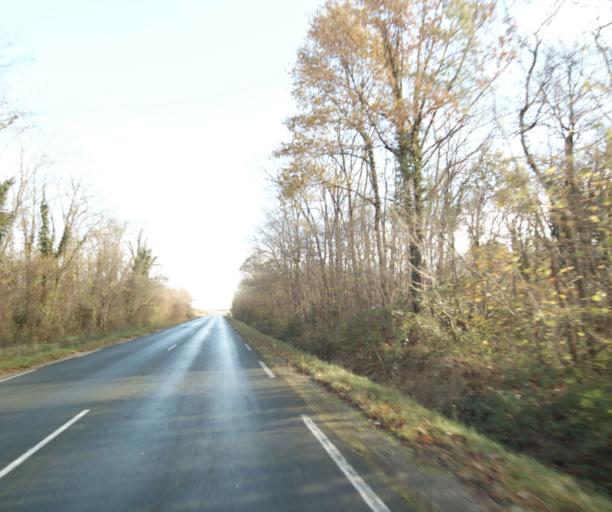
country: FR
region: Poitou-Charentes
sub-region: Departement de la Charente-Maritime
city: Saint-Romain-de-Benet
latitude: 45.6962
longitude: -0.8100
